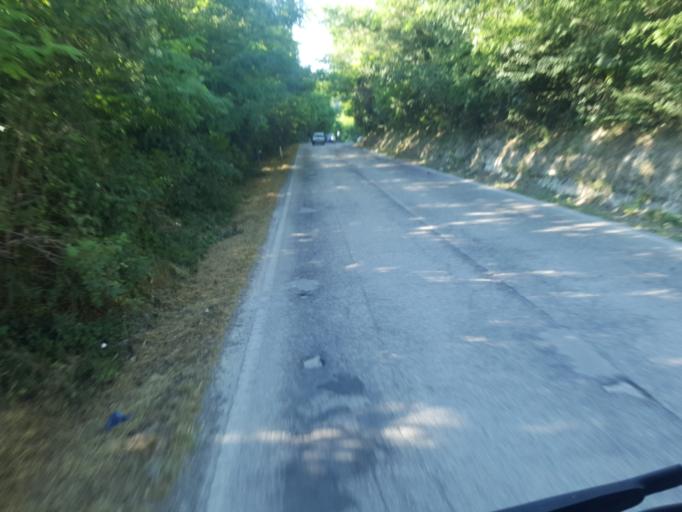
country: IT
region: The Marches
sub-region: Provincia di Pesaro e Urbino
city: Montecalvo in Foglia
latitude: 43.7908
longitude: 12.6217
